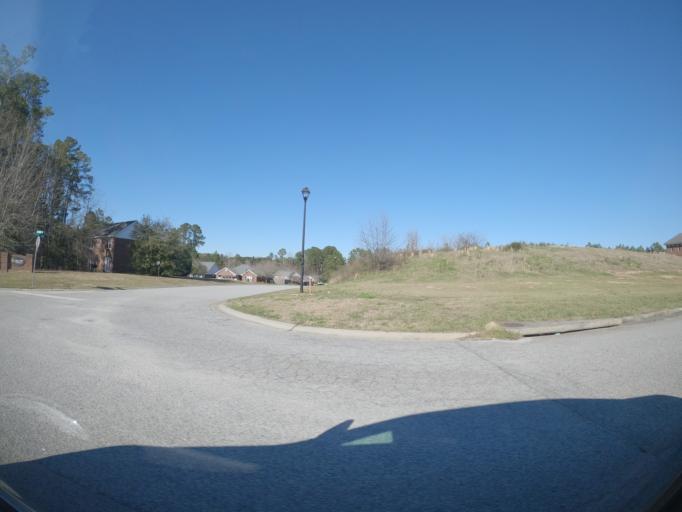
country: US
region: Georgia
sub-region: Columbia County
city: Grovetown
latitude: 33.4543
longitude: -82.2266
